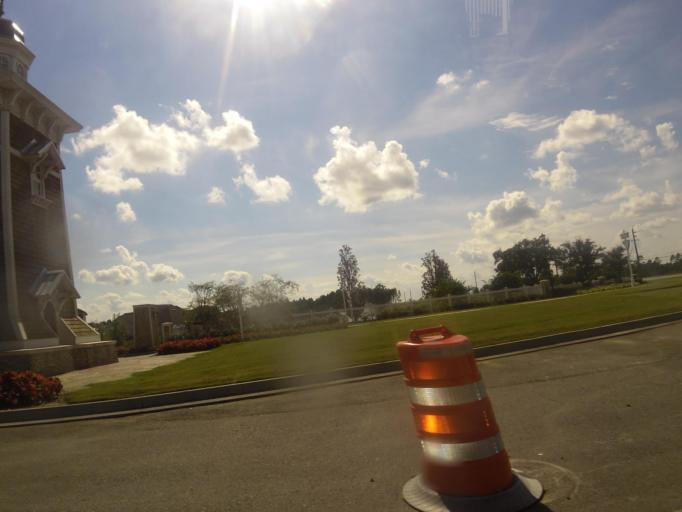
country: US
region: Florida
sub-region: Saint Johns County
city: Palm Valley
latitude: 30.0834
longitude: -81.4719
